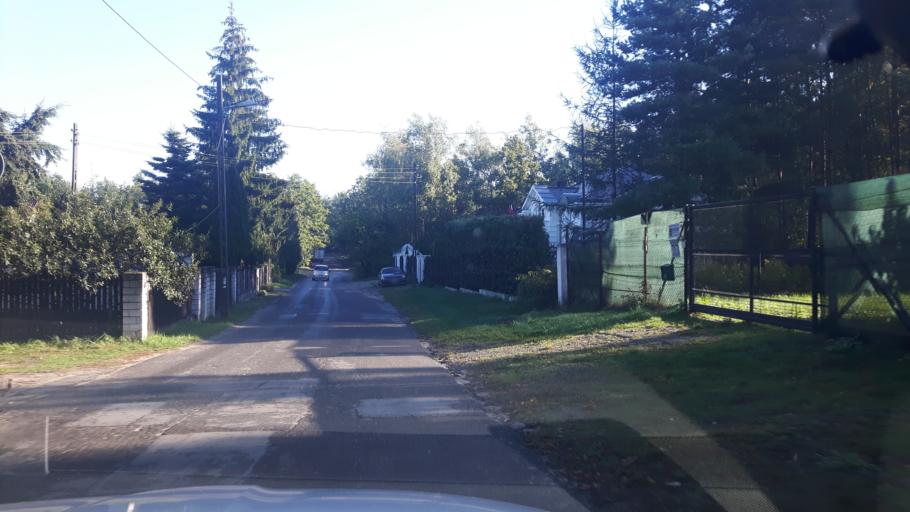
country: PL
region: Masovian Voivodeship
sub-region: Warszawa
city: Bialoleka
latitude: 52.3347
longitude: 21.0001
